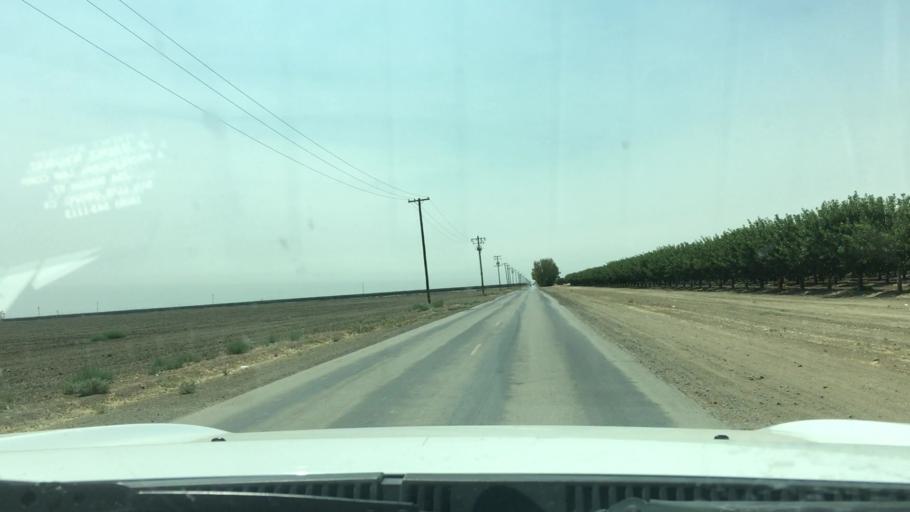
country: US
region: California
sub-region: Kern County
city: Wasco
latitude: 35.7092
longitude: -119.4373
